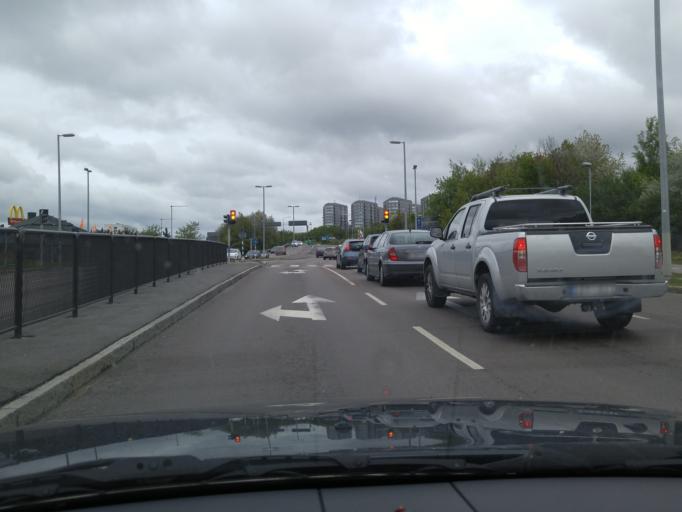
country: SE
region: Vaestra Goetaland
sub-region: Goteborg
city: Majorna
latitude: 57.6458
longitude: 11.9173
